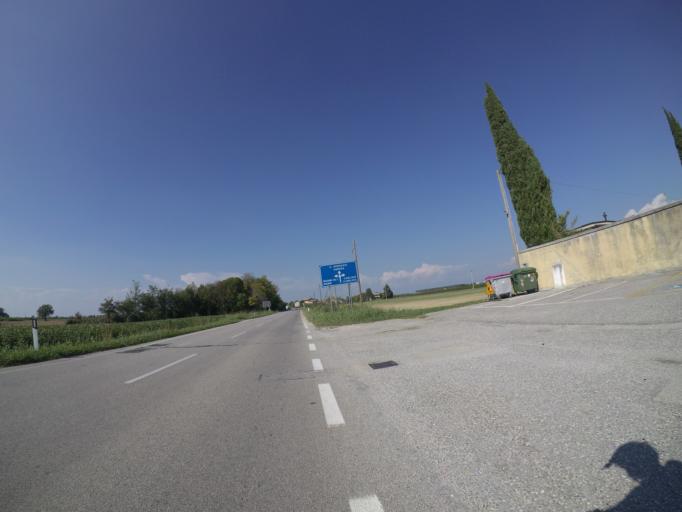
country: IT
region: Friuli Venezia Giulia
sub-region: Provincia di Udine
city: Carlino
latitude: 45.8057
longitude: 13.1652
